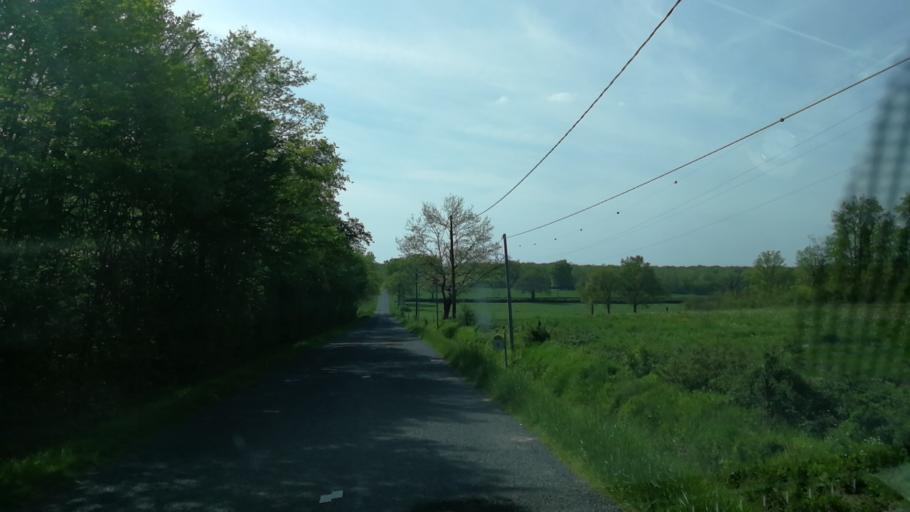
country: FR
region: Auvergne
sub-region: Departement de l'Allier
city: Neuilly-le-Real
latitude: 46.5141
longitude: 3.4541
